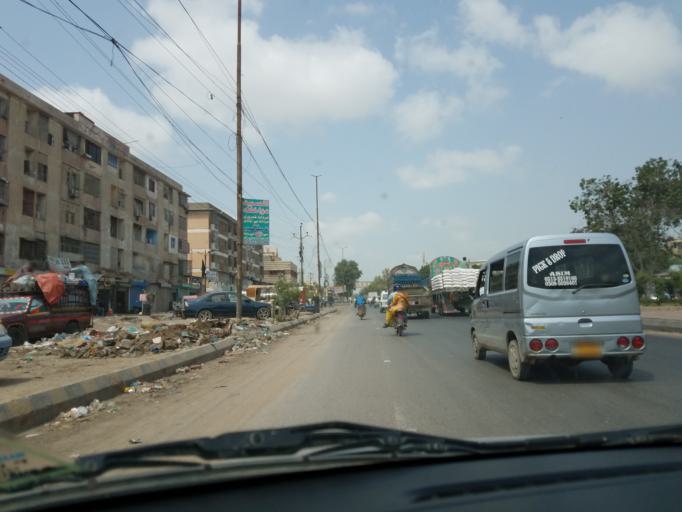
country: PK
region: Sindh
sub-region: Karachi District
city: Karachi
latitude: 24.9479
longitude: 67.0824
